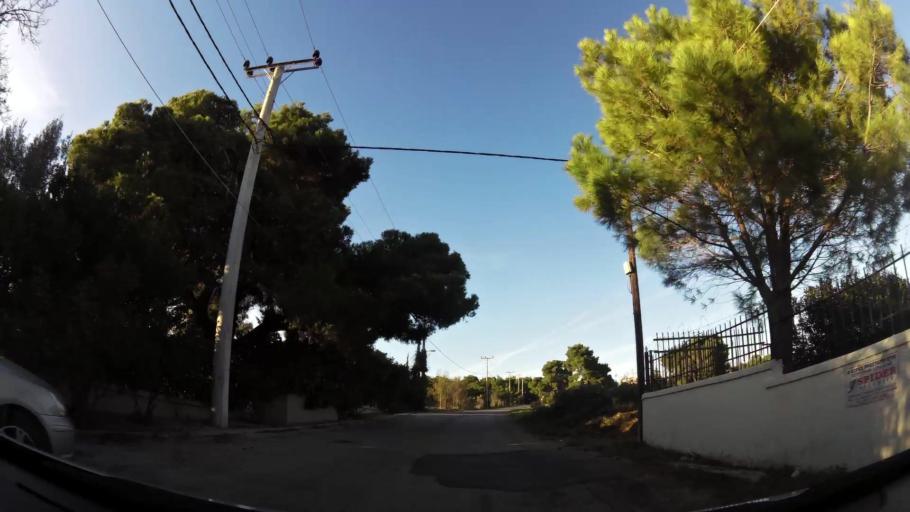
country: GR
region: Attica
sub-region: Nomarchia Anatolikis Attikis
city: Kryoneri
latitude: 38.1311
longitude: 23.8247
